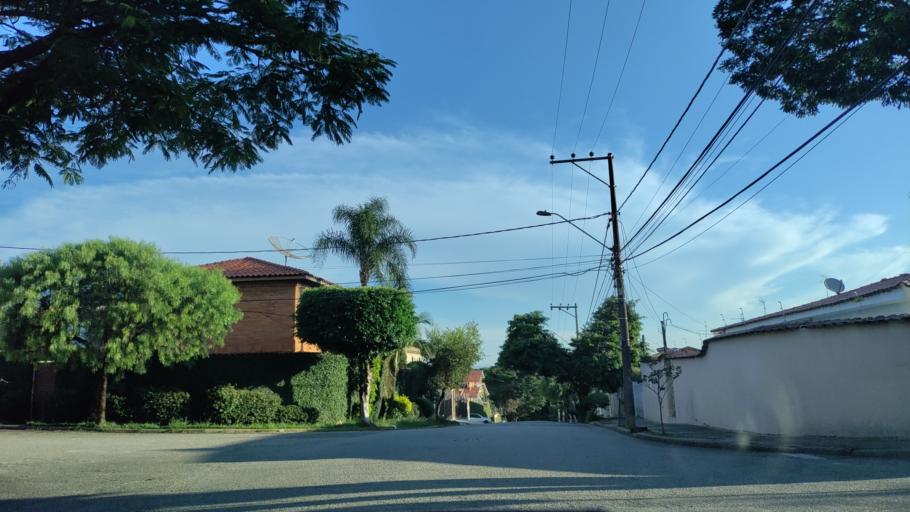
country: BR
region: Sao Paulo
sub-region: Sorocaba
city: Sorocaba
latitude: -23.5078
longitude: -47.4901
